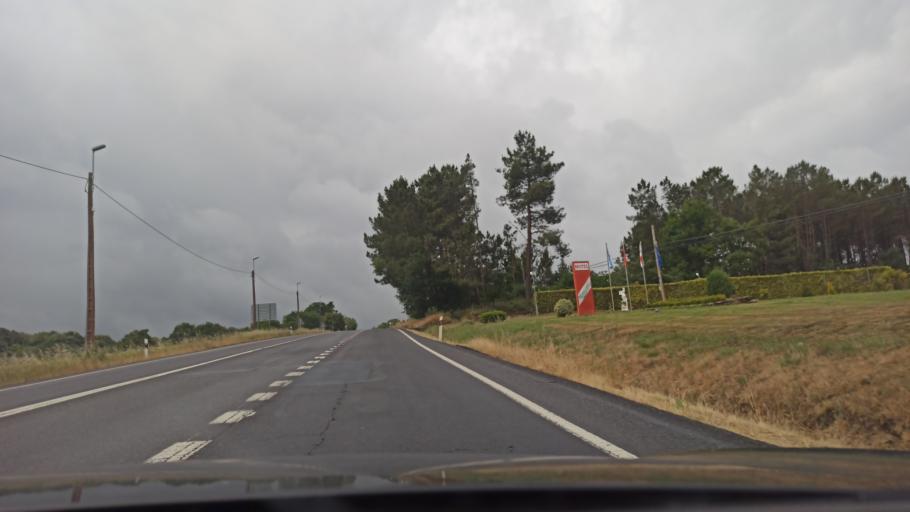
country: ES
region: Galicia
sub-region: Provincia de Lugo
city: Lugo
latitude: 42.9700
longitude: -7.5955
